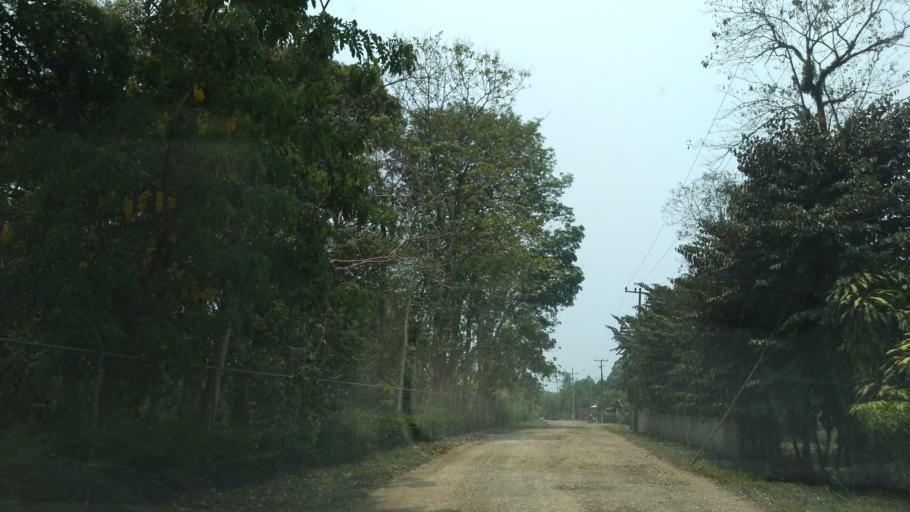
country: MX
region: Veracruz
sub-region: Tezonapa
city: Laguna Chica (Pueblo Nuevo)
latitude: 18.5155
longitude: -96.7627
